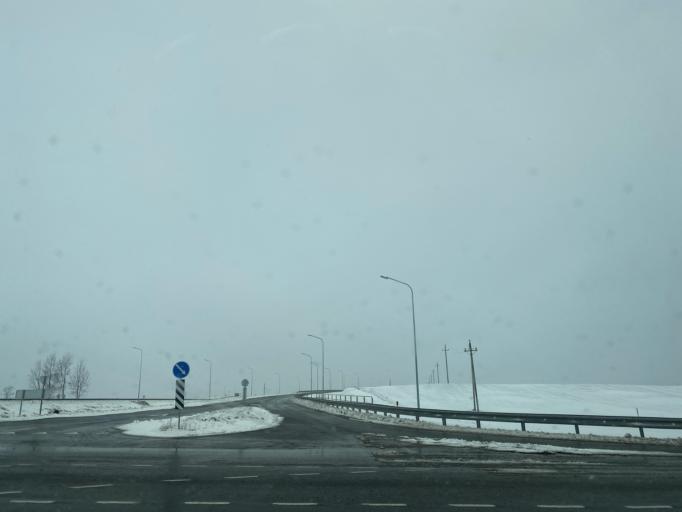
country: BY
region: Minsk
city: Slabada
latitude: 54.0227
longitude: 27.9316
